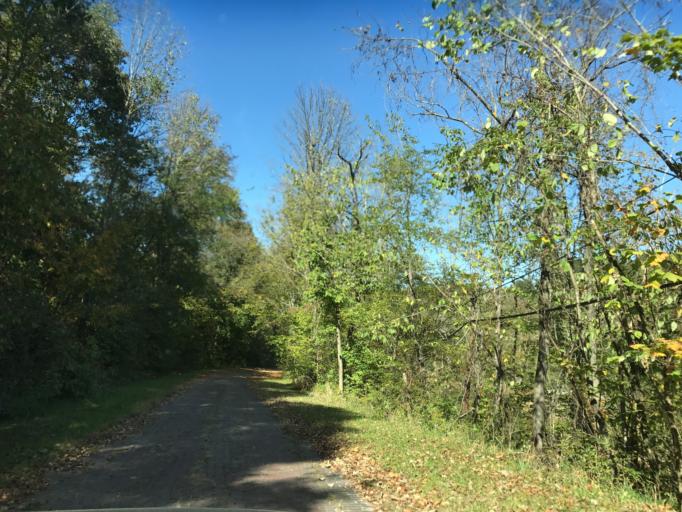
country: US
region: Ohio
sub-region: Guernsey County
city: Byesville
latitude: 40.0298
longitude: -81.4942
